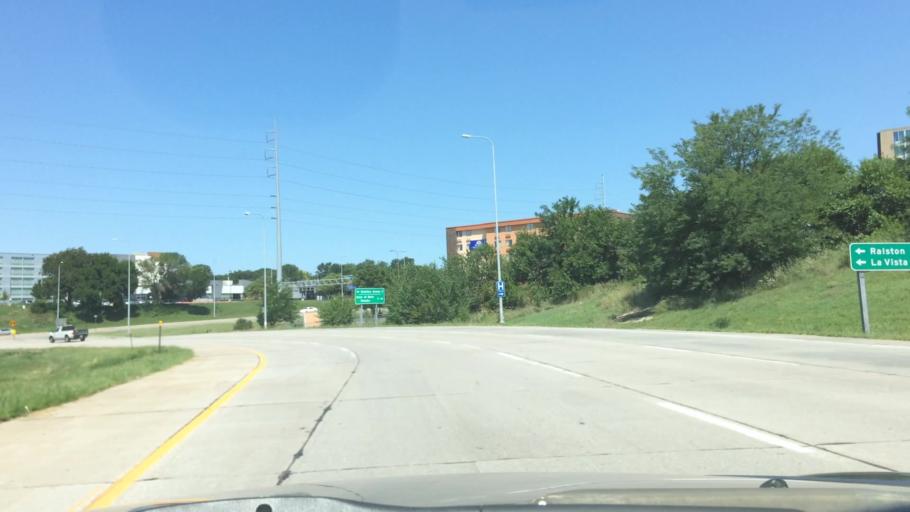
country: US
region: Nebraska
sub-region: Douglas County
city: Ralston
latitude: 41.2246
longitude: -96.0222
